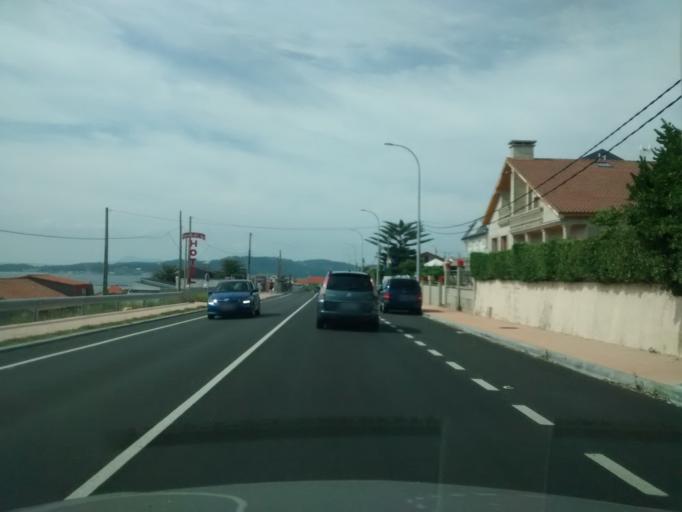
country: ES
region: Galicia
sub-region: Provincia de Pontevedra
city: O Grove
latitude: 42.4261
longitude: -8.8720
